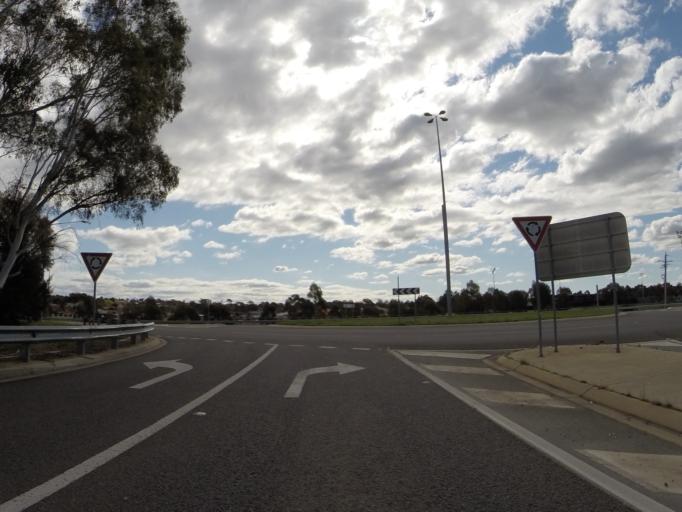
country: AU
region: Australian Capital Territory
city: Belconnen
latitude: -35.2165
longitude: 149.0847
